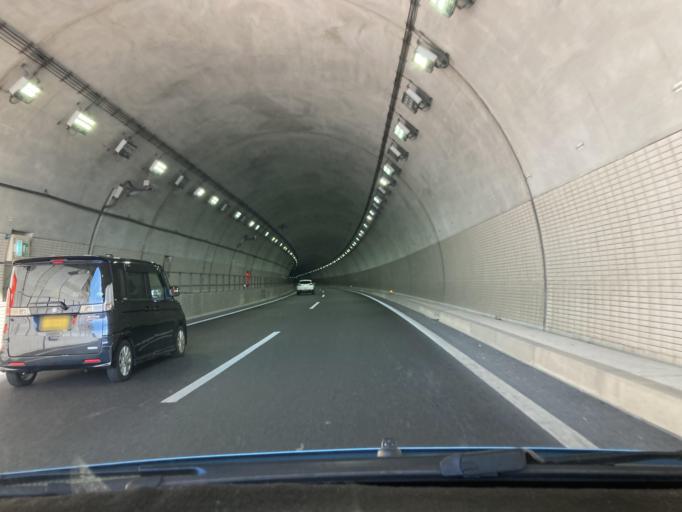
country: JP
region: Okinawa
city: Tomigusuku
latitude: 26.1714
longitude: 127.6805
